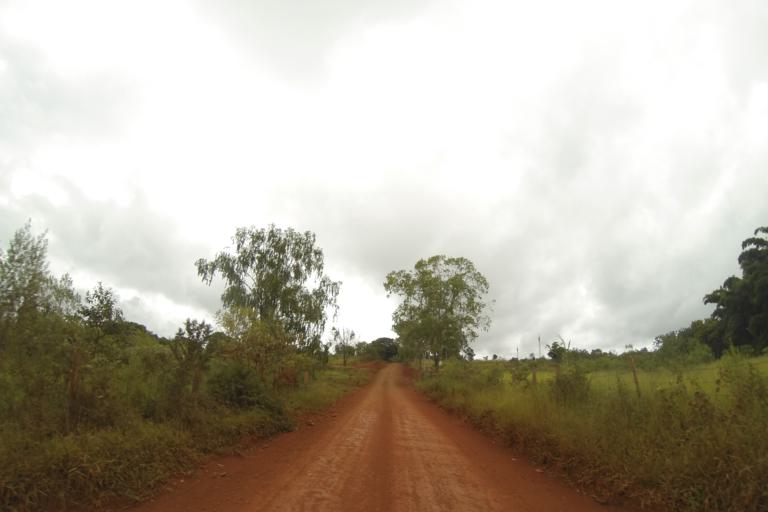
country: BR
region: Minas Gerais
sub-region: Campos Altos
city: Campos Altos
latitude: -19.8697
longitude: -46.3054
